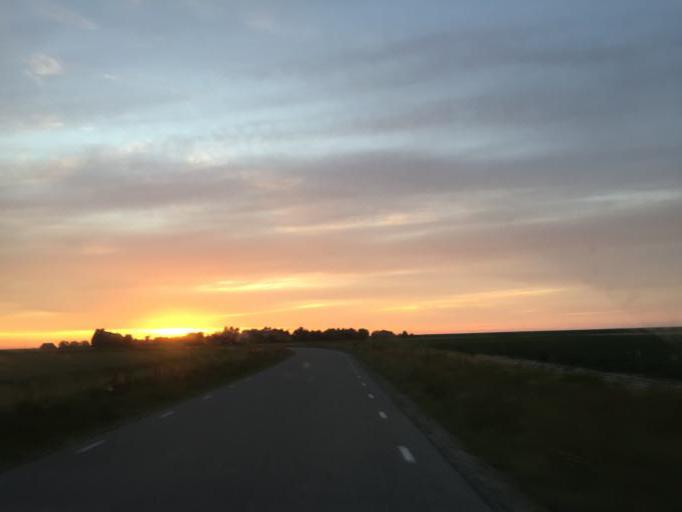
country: NL
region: Friesland
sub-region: Gemeente Dongeradeel
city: Anjum
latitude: 53.3930
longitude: 6.0992
